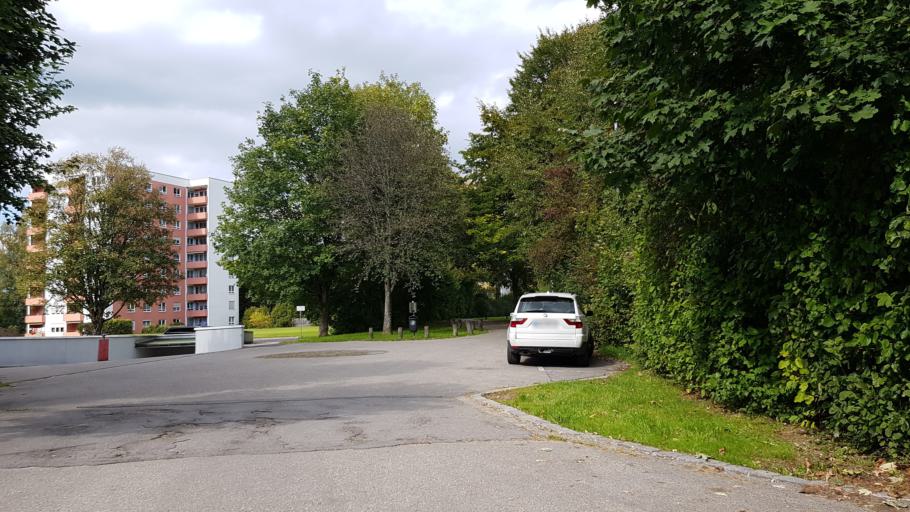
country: DE
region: Bavaria
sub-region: Swabia
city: Fuessen
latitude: 47.5736
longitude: 10.6845
